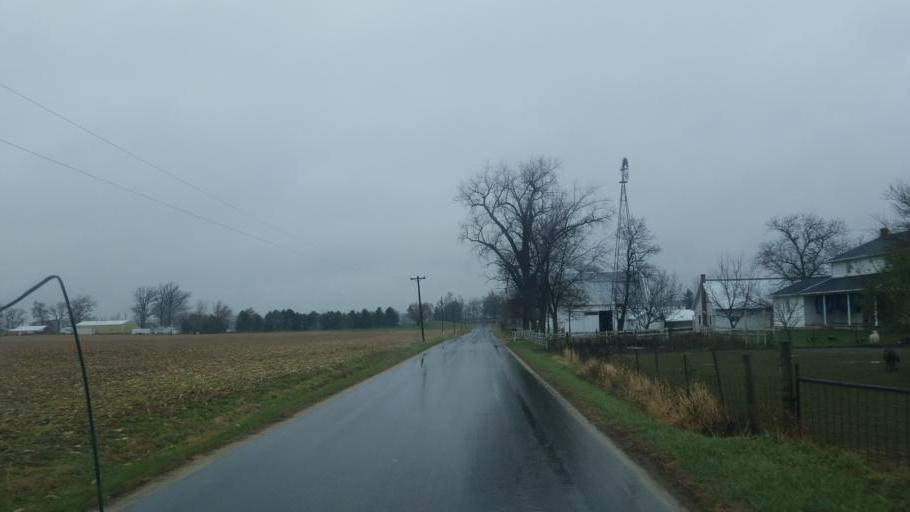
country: US
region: Indiana
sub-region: Adams County
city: Berne
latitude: 40.6552
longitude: -84.8976
